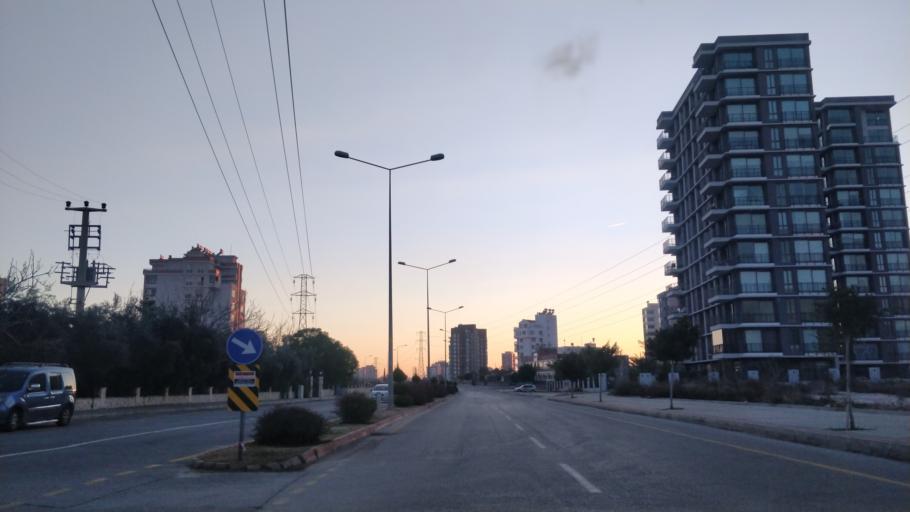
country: TR
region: Mersin
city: Mercin
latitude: 36.8049
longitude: 34.5724
